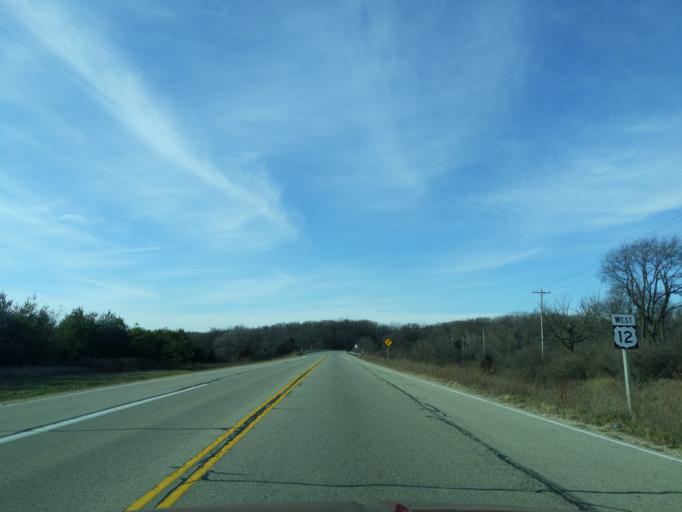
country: US
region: Wisconsin
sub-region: Jefferson County
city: Palmyra
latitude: 42.7984
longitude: -88.6418
